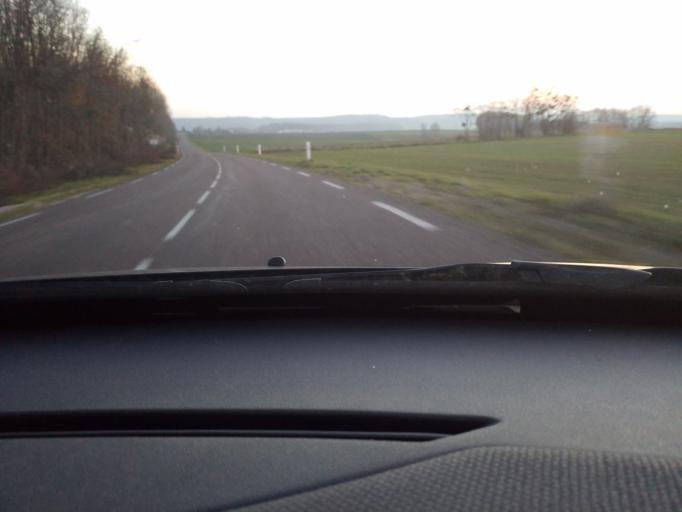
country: FR
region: Franche-Comte
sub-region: Departement de la Haute-Saone
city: Faverney
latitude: 47.8968
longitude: 6.0732
